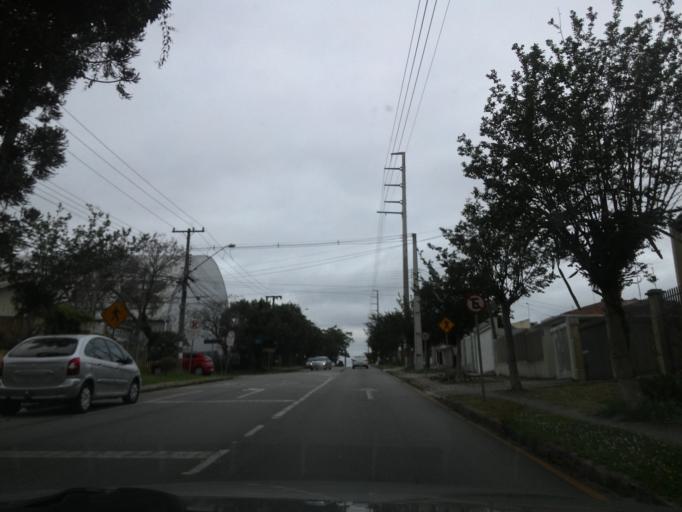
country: BR
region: Parana
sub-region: Pinhais
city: Pinhais
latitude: -25.4581
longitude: -49.2373
